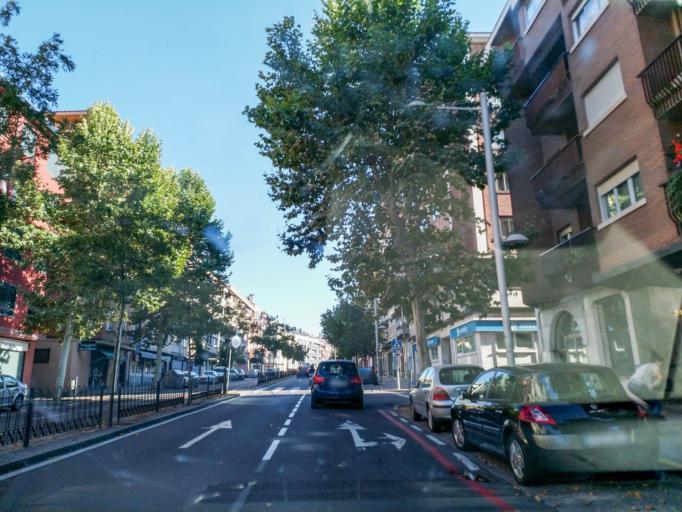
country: ES
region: Castille and Leon
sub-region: Provincia de Segovia
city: Segovia
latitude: 40.9386
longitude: -4.1151
